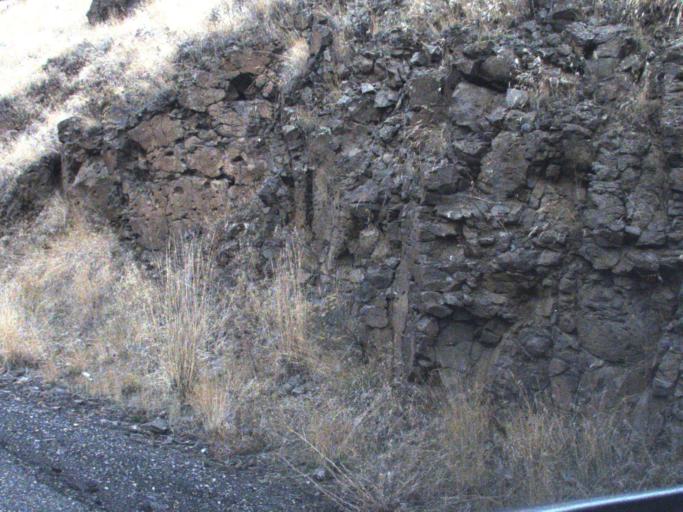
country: US
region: Washington
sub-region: Garfield County
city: Pomeroy
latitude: 46.4403
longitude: -117.3710
